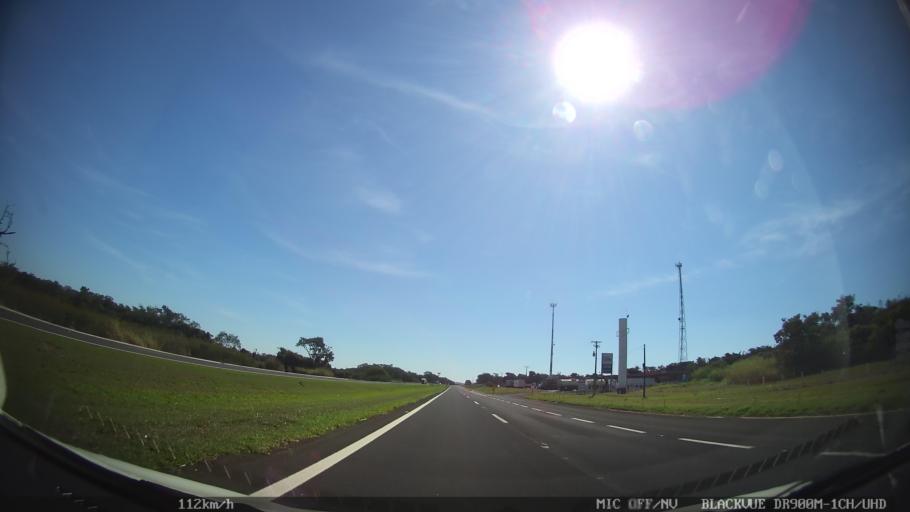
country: BR
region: Sao Paulo
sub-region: Sao Simao
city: Sao Simao
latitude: -21.5560
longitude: -47.6364
